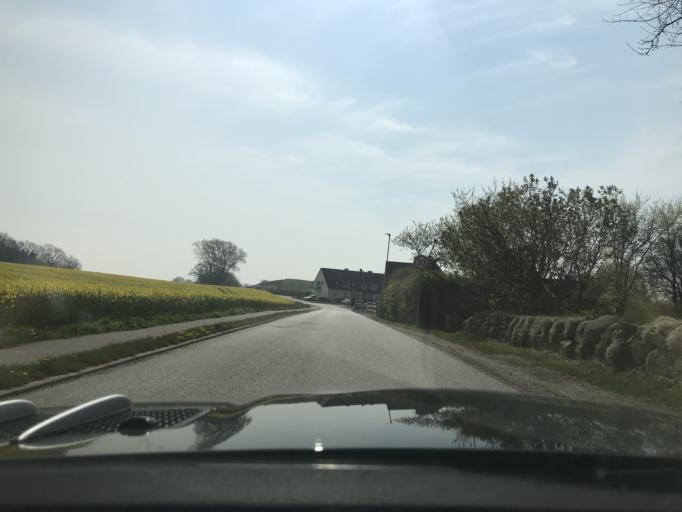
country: DE
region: Schleswig-Holstein
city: Schashagen
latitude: 54.1297
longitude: 10.9137
